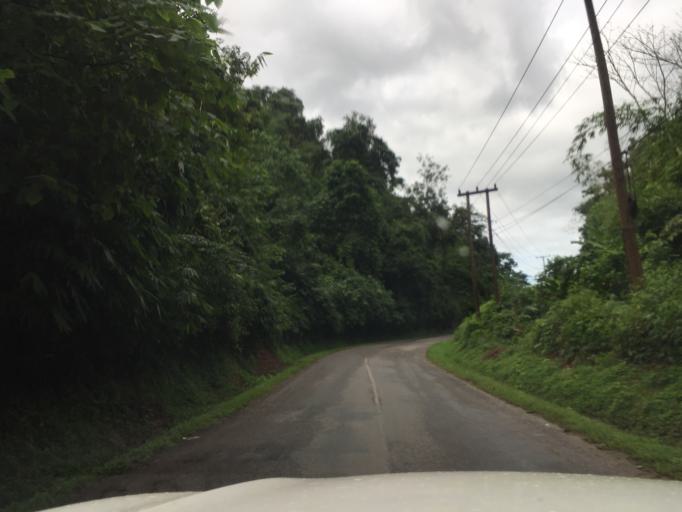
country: LA
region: Oudomxai
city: Muang La
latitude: 20.8030
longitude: 102.0877
